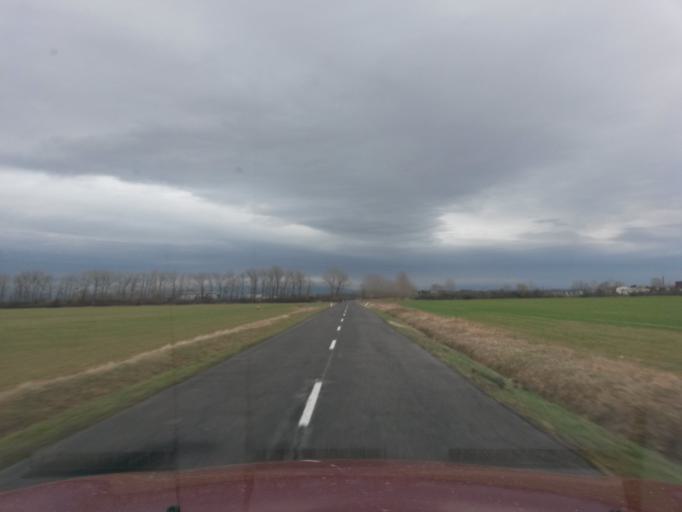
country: SK
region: Kosicky
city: Michalovce
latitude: 48.6633
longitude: 22.0024
